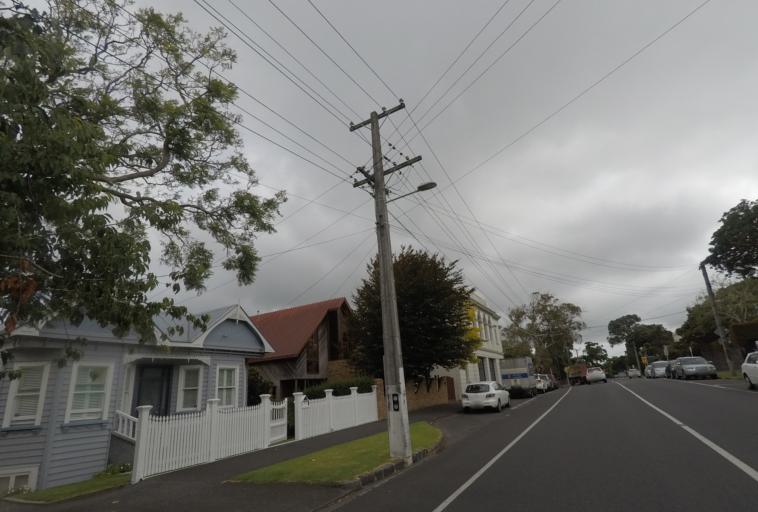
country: NZ
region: Auckland
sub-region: Auckland
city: Auckland
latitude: -36.8781
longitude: 174.7570
